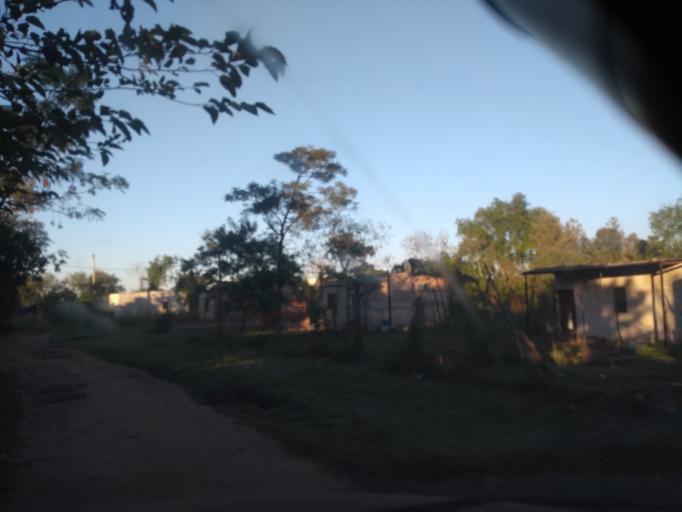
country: AR
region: Chaco
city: Resistencia
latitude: -27.4589
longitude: -58.9690
